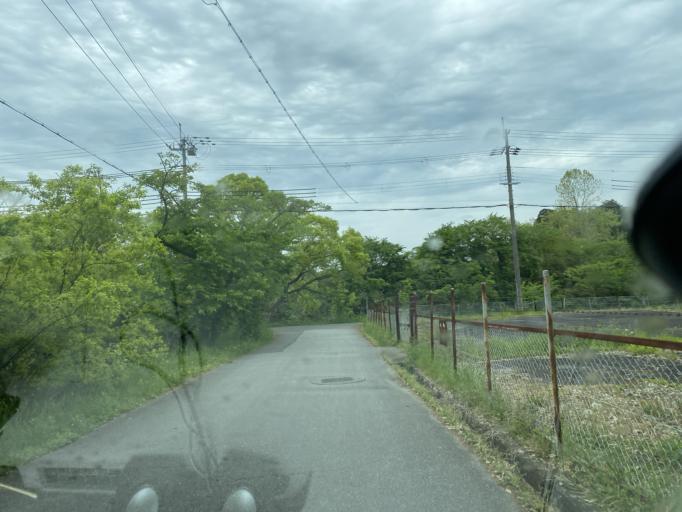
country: JP
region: Hyogo
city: Sasayama
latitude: 35.0708
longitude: 135.2171
